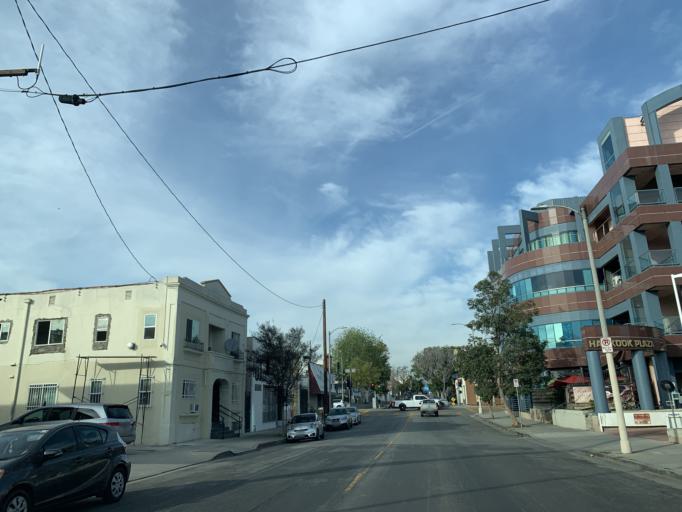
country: US
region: California
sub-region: Los Angeles County
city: Silver Lake
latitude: 34.0519
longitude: -118.3041
